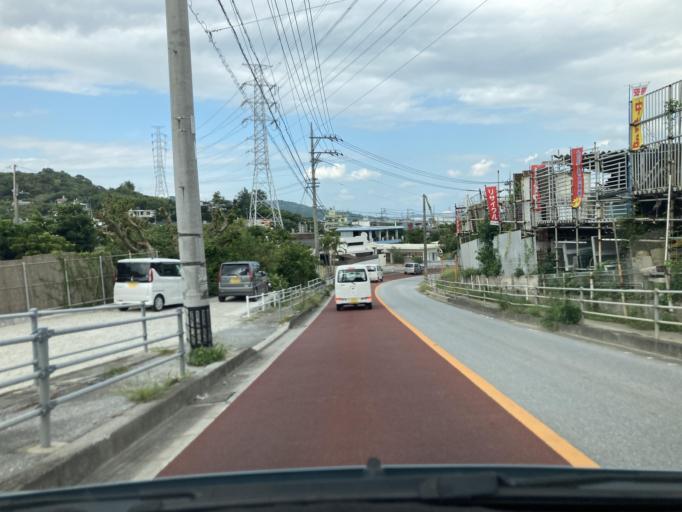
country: JP
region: Okinawa
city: Ginowan
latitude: 26.2537
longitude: 127.7830
